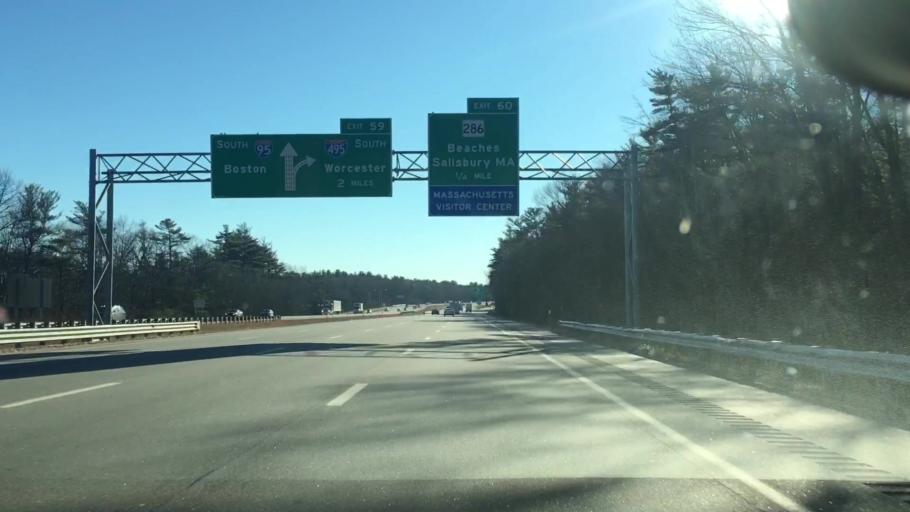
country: US
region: New Hampshire
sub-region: Rockingham County
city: Seabrook
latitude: 42.8869
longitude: -70.8819
